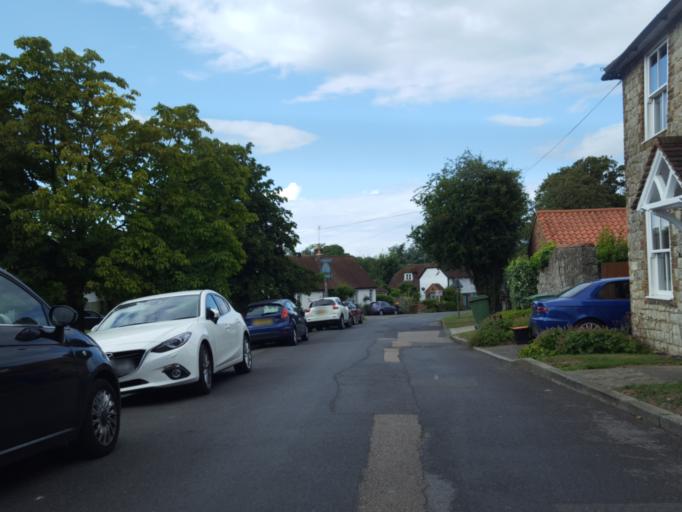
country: GB
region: England
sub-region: Kent
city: Maidstone
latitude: 51.2336
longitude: 0.5313
